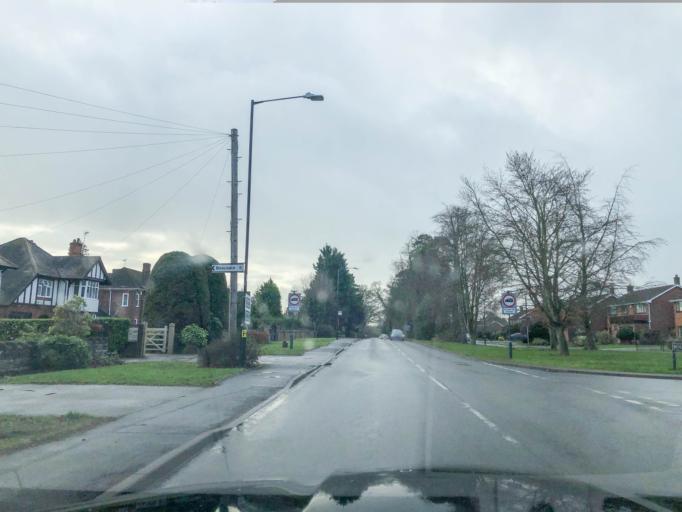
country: GB
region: England
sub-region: Warwickshire
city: Kenilworth
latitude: 52.3337
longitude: -1.5733
